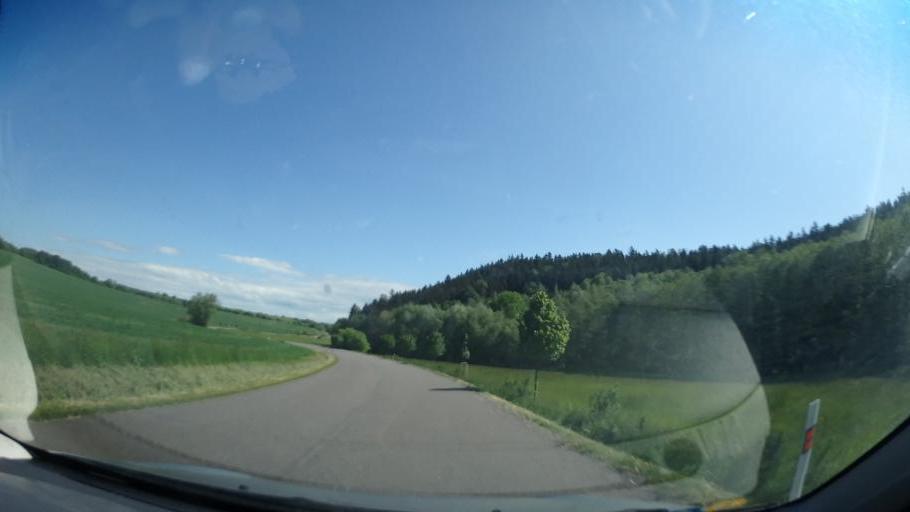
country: CZ
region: South Moravian
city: Velke Opatovice
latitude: 49.6400
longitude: 16.6137
